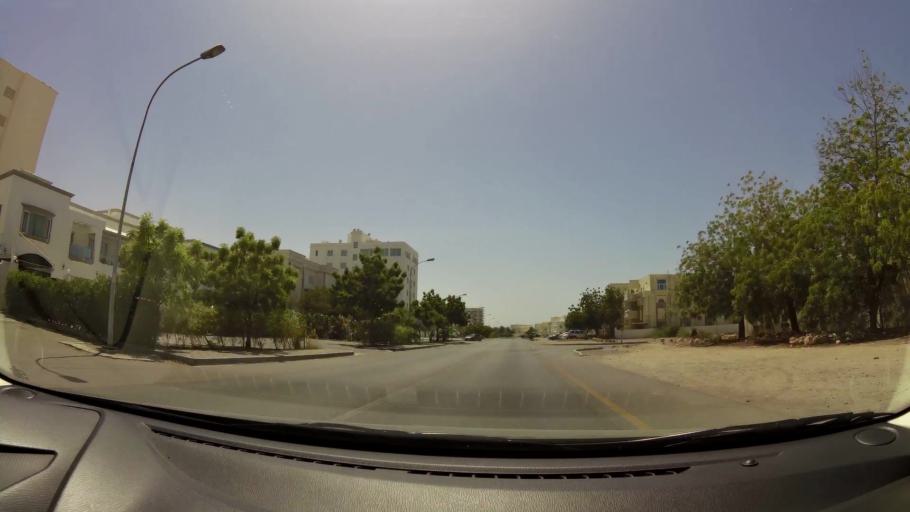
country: OM
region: Muhafazat Masqat
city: Bawshar
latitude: 23.5952
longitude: 58.3642
